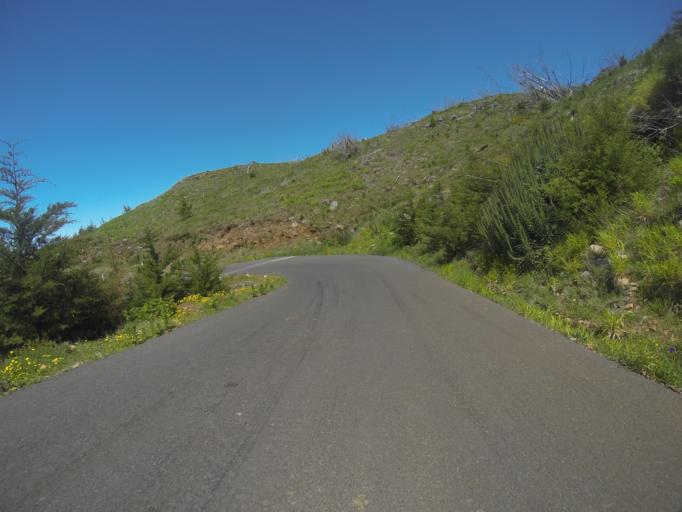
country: PT
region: Madeira
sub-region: Funchal
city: Nossa Senhora do Monte
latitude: 32.7030
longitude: -16.9146
